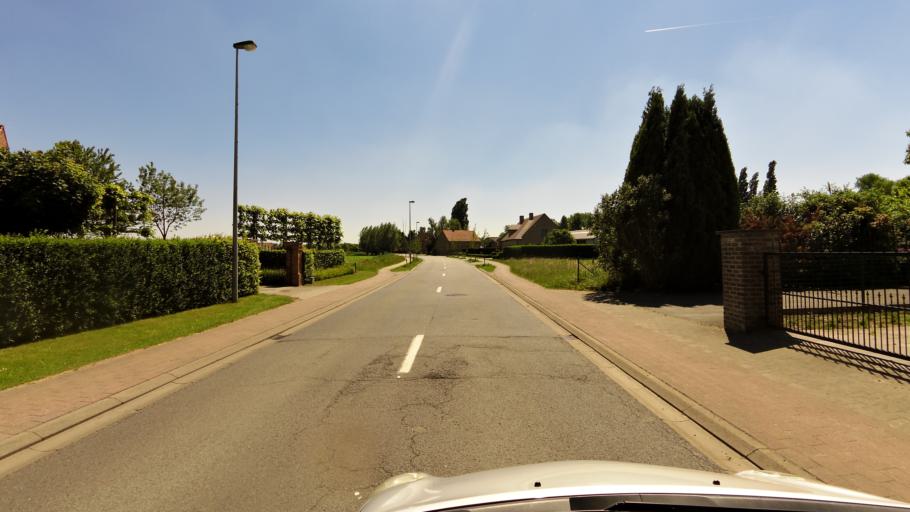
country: BE
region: Flanders
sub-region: Provincie West-Vlaanderen
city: Oostkamp
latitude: 51.1298
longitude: 3.2612
